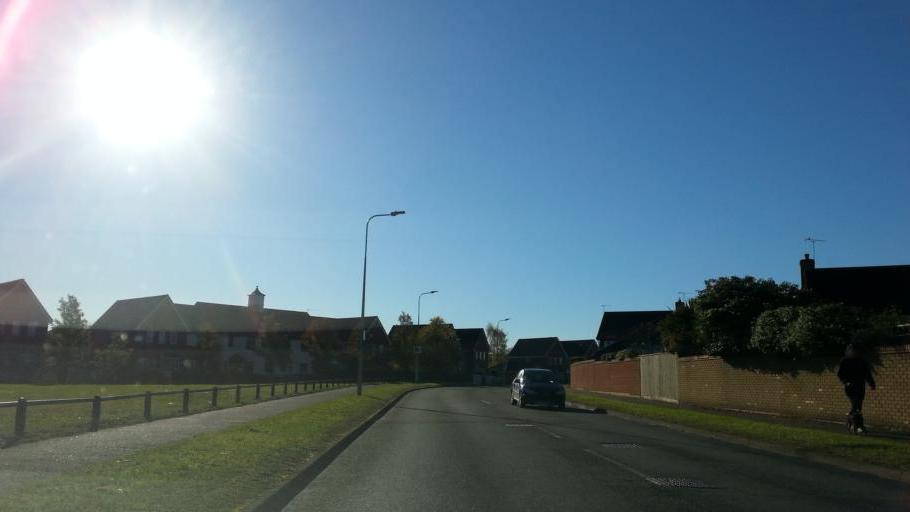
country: GB
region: England
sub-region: Suffolk
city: Kesgrave
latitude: 52.0613
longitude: 1.2535
